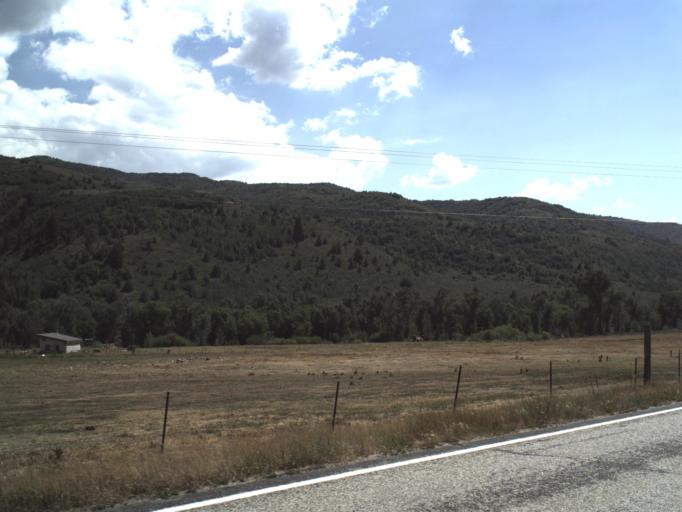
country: US
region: Utah
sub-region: Weber County
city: Wolf Creek
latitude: 41.2971
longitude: -111.6203
